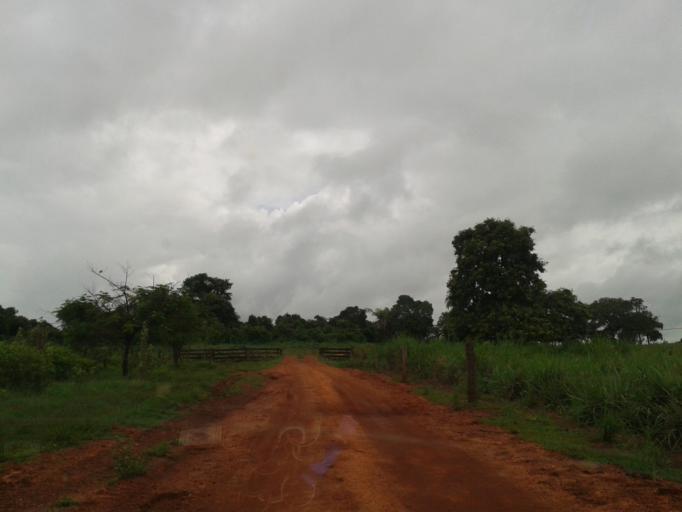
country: BR
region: Minas Gerais
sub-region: Santa Vitoria
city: Santa Vitoria
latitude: -18.7364
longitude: -49.9854
